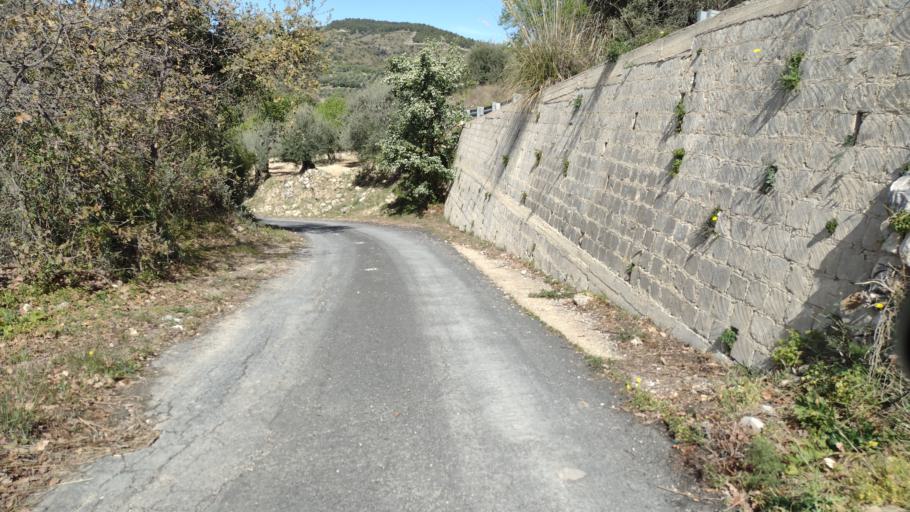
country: IT
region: Sicily
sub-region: Provincia di Siracusa
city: Noto
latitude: 36.9042
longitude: 15.0203
